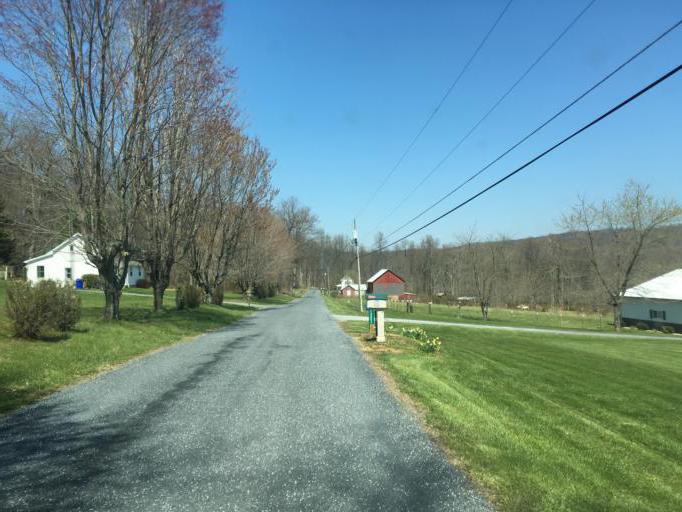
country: US
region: Maryland
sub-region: Washington County
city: Smithsburg
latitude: 39.6175
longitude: -77.5346
